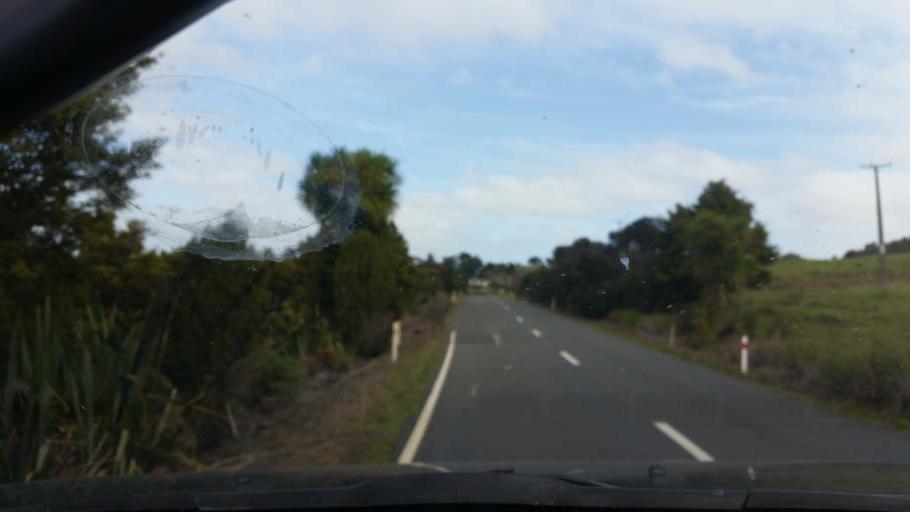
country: NZ
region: Northland
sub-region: Kaipara District
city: Dargaville
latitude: -35.8843
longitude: 173.8430
